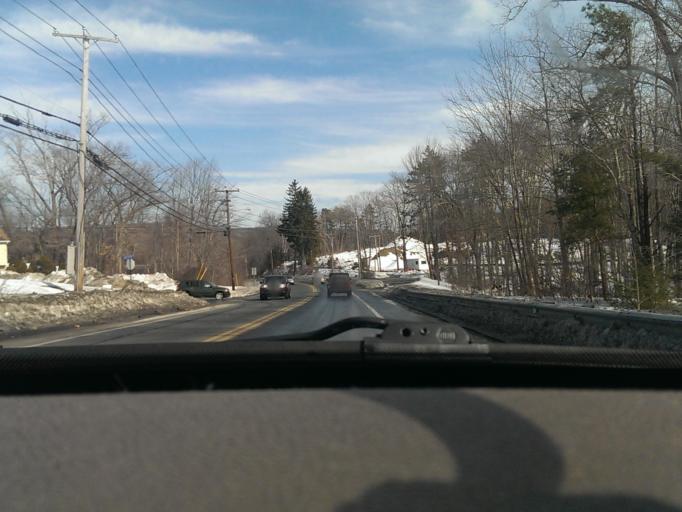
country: US
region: Massachusetts
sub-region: Hampden County
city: Three Rivers
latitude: 42.1608
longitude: -72.3533
